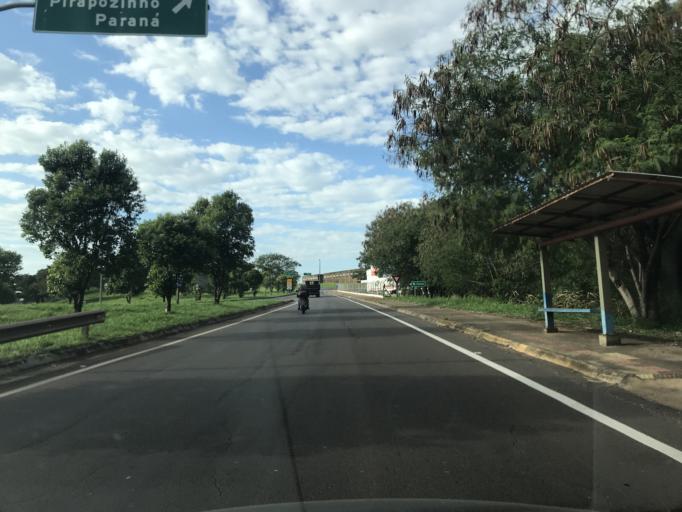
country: BR
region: Sao Paulo
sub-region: Presidente Prudente
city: Presidente Prudente
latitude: -22.1497
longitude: -51.3913
